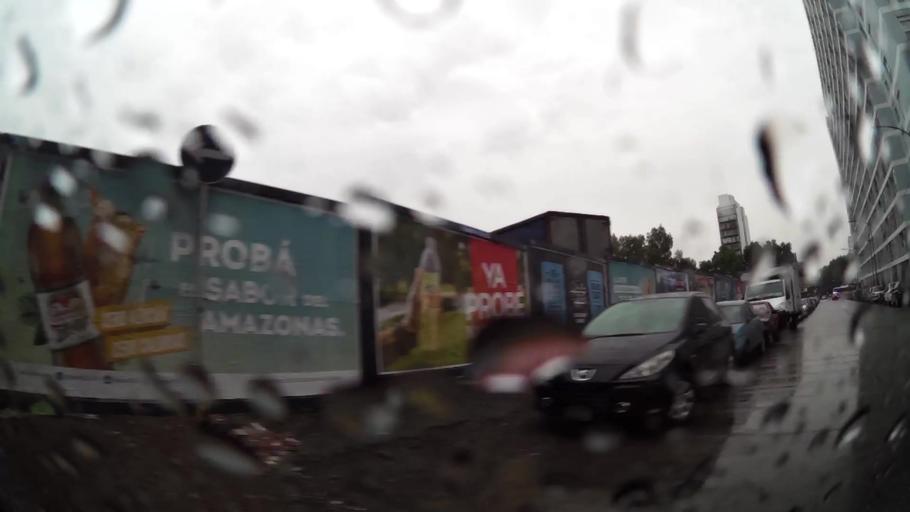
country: AR
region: Buenos Aires F.D.
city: Buenos Aires
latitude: -34.6292
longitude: -58.3674
